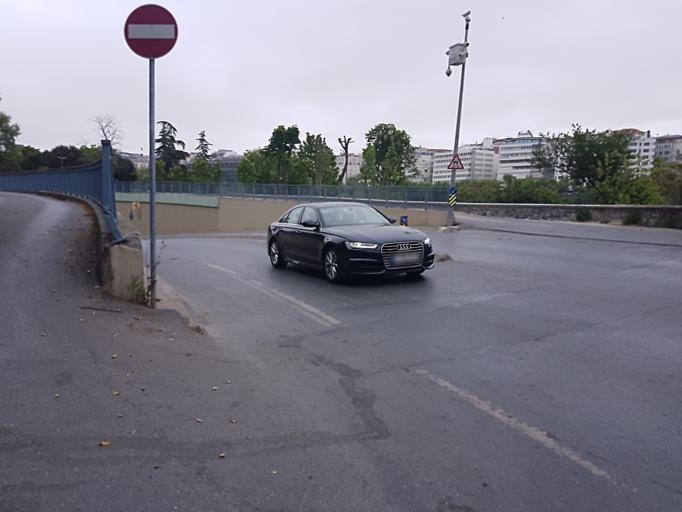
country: TR
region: Istanbul
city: Sisli
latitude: 41.0442
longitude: 28.9906
